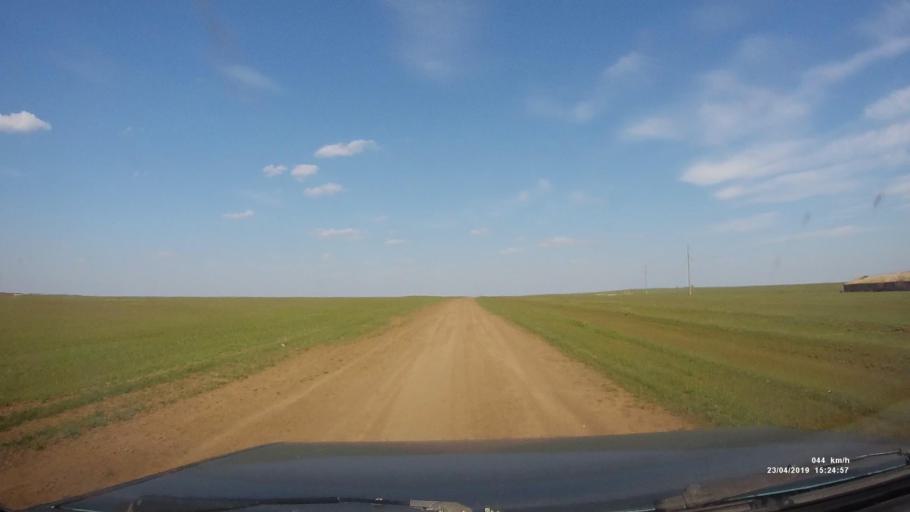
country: RU
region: Rostov
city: Remontnoye
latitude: 46.5406
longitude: 42.9765
